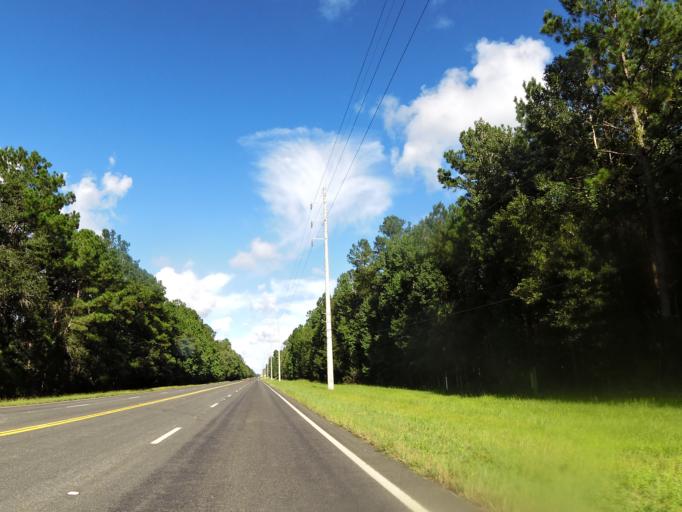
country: US
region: Georgia
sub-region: Camden County
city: Woodbine
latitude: 31.1009
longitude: -81.7035
